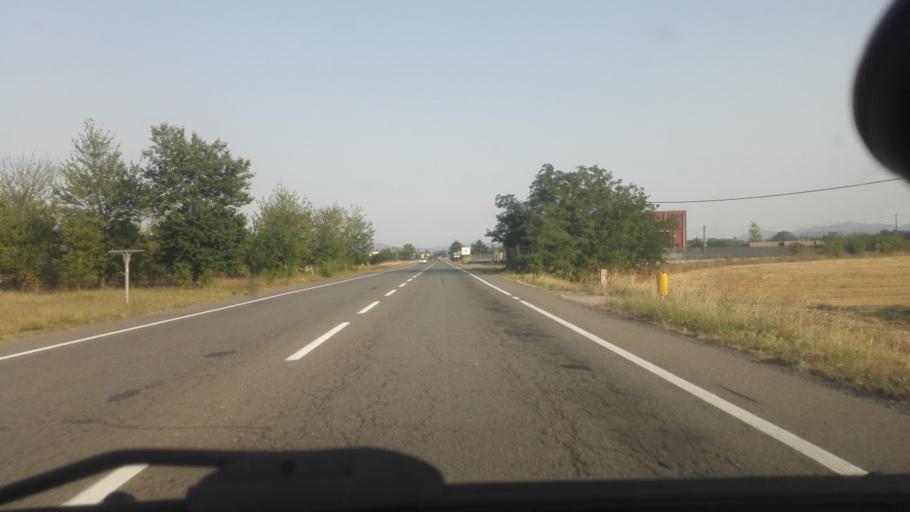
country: IT
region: Piedmont
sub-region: Provincia di Alessandria
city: Pozzolo Formigaro
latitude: 44.8076
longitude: 8.7681
